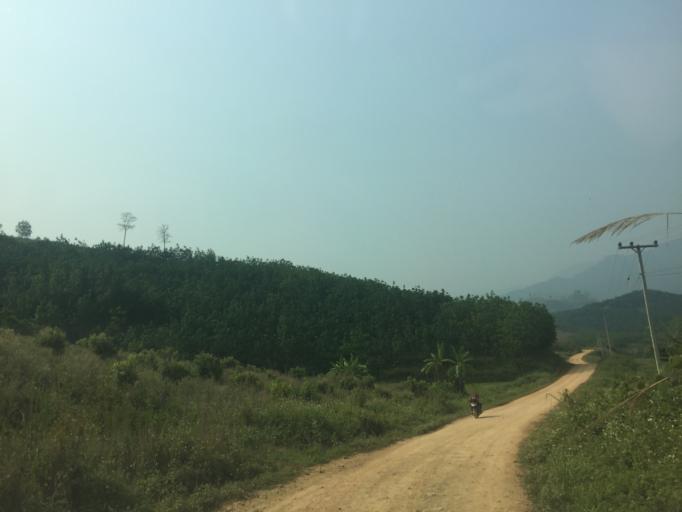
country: TH
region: Phayao
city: Phu Sang
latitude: 19.6463
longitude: 100.5256
